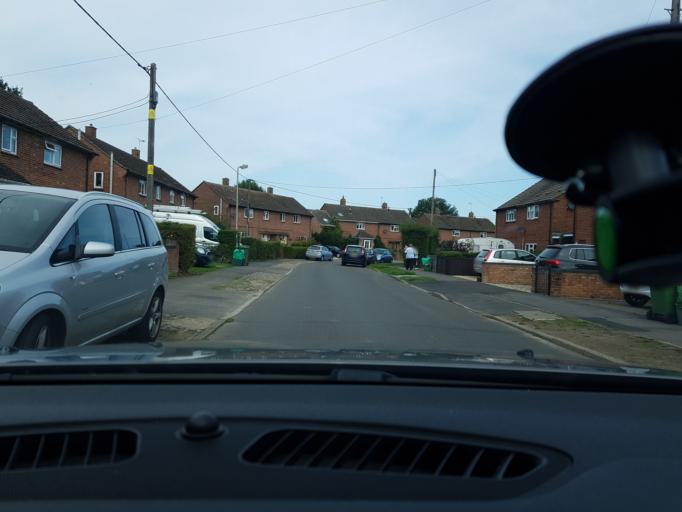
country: GB
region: England
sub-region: West Berkshire
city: Hungerford
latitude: 51.4063
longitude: -1.5132
